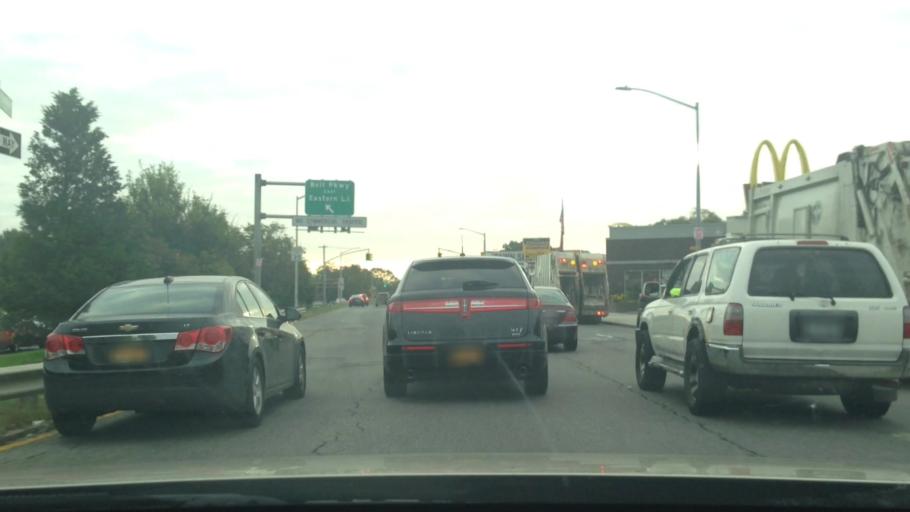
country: US
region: New York
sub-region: Nassau County
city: South Valley Stream
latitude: 40.6655
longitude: -73.7570
